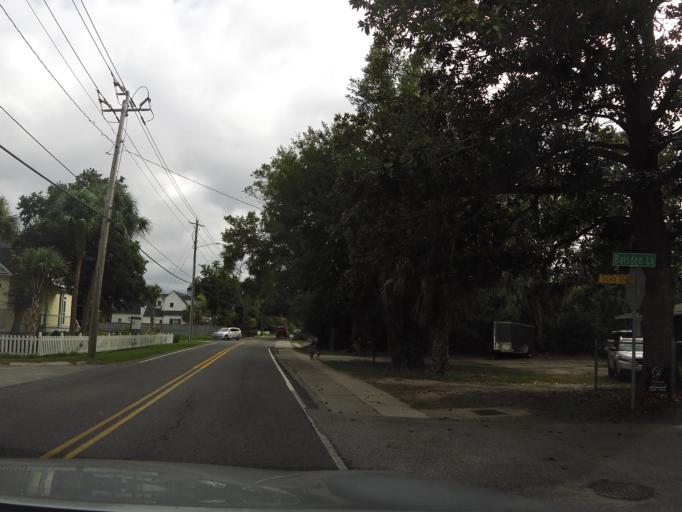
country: US
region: Georgia
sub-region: Glynn County
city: Saint Simons Island
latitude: 31.1454
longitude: -81.3827
